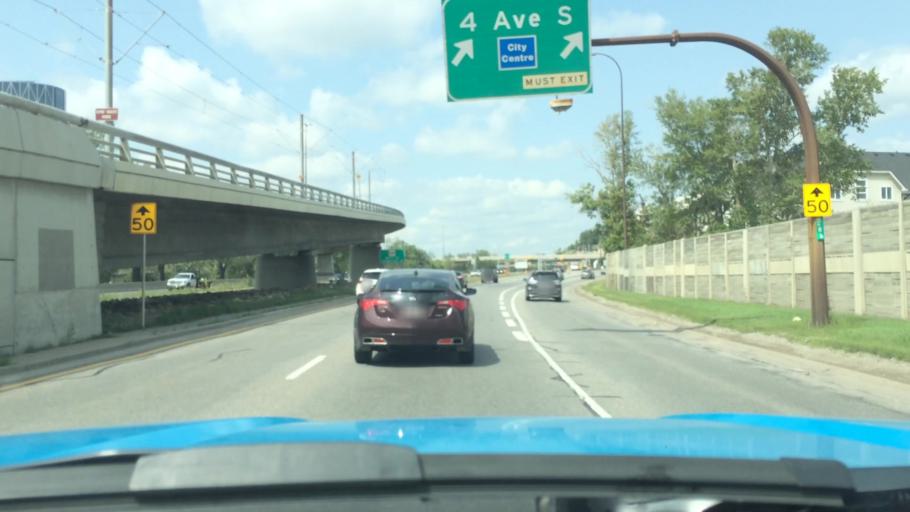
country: CA
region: Alberta
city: Calgary
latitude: 51.0495
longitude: -114.0459
